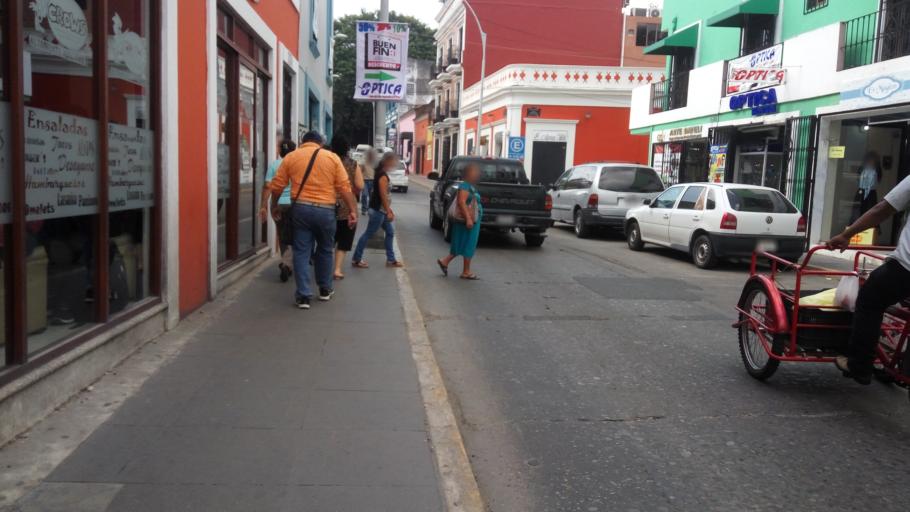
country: MX
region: Tabasco
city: Villahermosa
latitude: 17.9910
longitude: -92.9191
